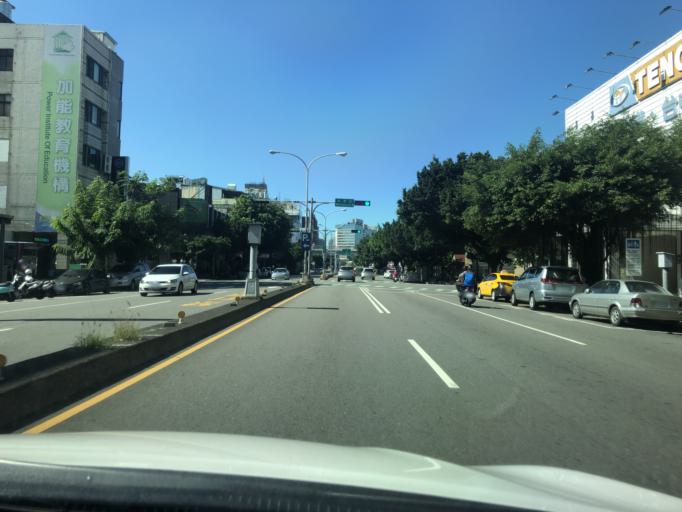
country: TW
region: Taiwan
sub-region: Taichung City
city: Taichung
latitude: 24.1609
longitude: 120.6850
